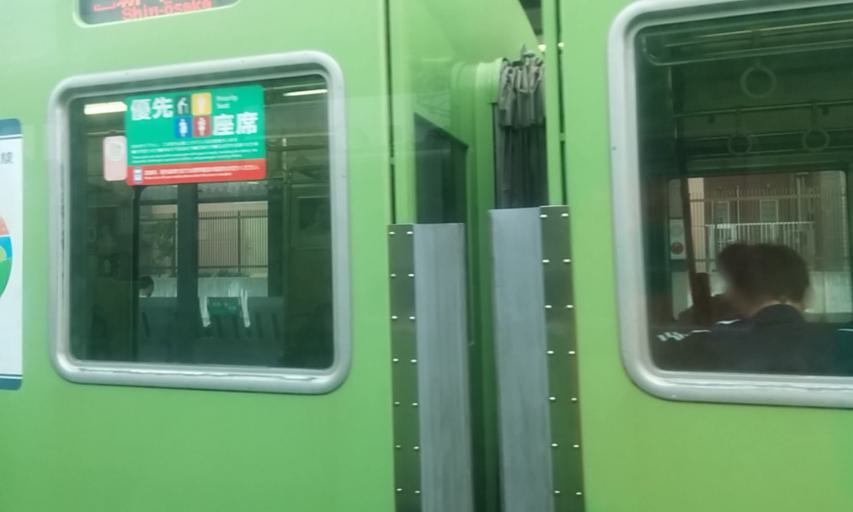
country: JP
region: Osaka
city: Moriguchi
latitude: 34.6879
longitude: 135.5635
